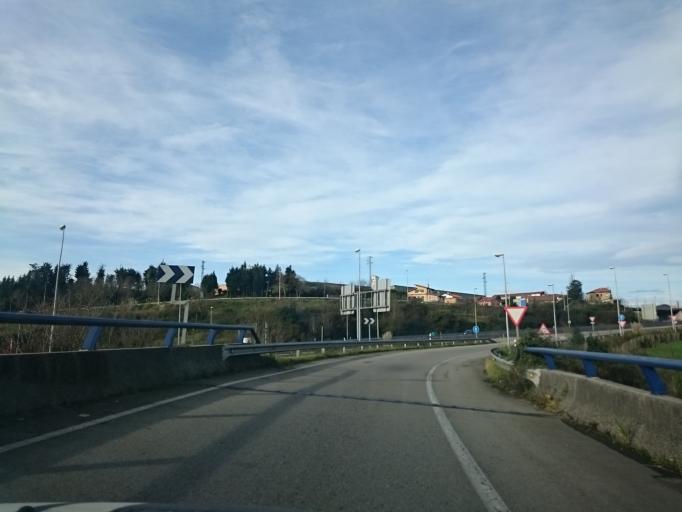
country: ES
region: Asturias
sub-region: Province of Asturias
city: Gijon
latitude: 43.5213
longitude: -5.6469
